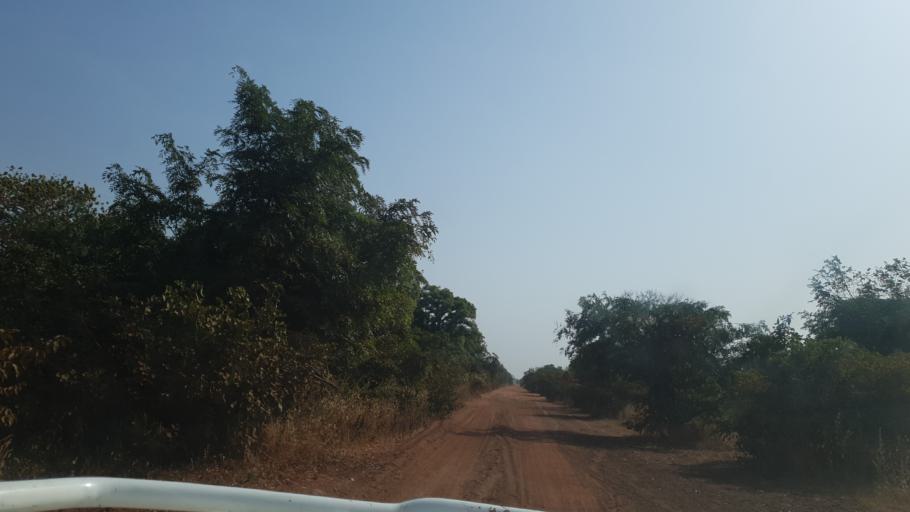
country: ML
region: Koulikoro
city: Dioila
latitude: 12.6684
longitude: -6.6827
